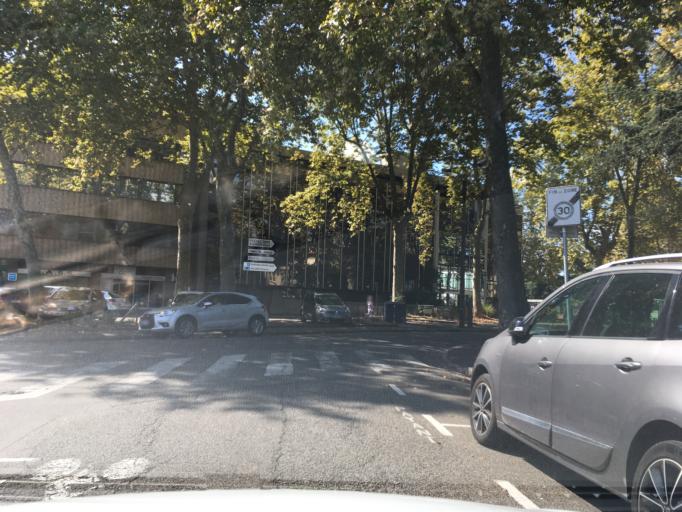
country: FR
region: Aquitaine
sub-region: Departement du Lot-et-Garonne
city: Agen
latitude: 44.2010
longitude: 0.6181
